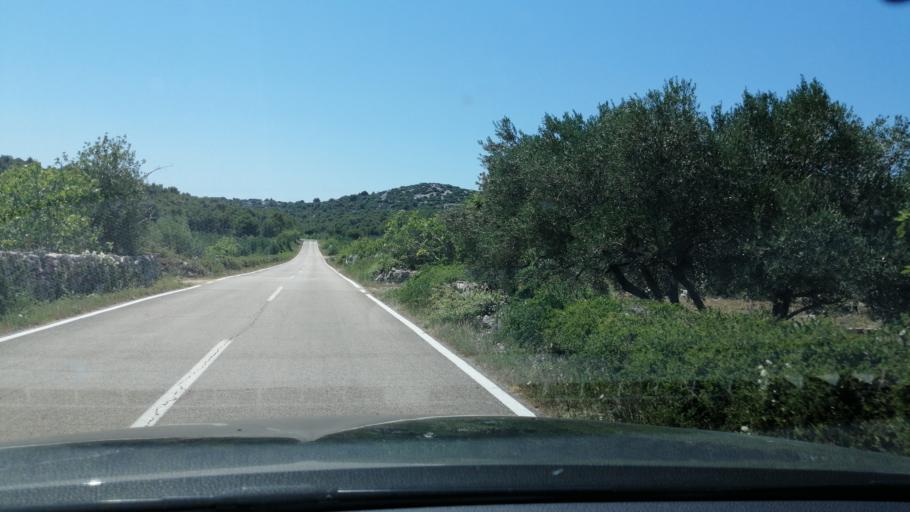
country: HR
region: Sibensko-Kniniska
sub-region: Grad Sibenik
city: Pirovac
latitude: 43.8486
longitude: 15.6871
